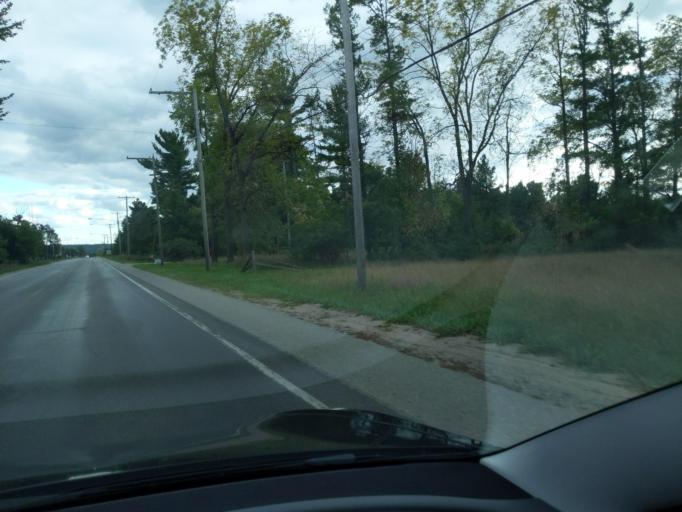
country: US
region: Michigan
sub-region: Kalkaska County
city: Rapid City
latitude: 44.8264
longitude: -85.2828
